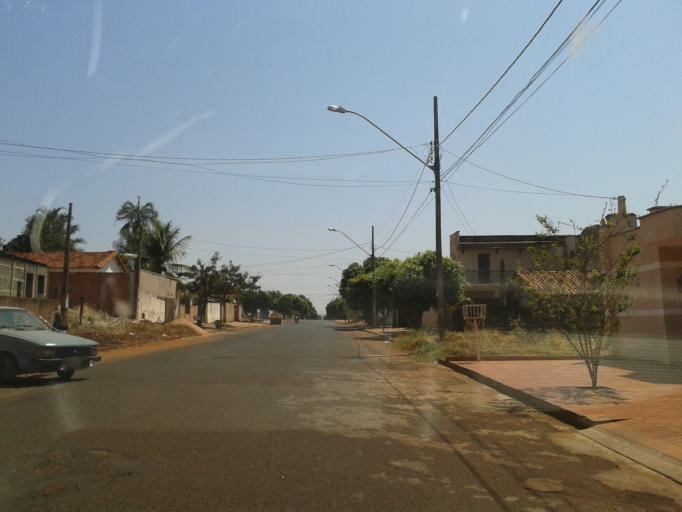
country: BR
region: Minas Gerais
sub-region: Ituiutaba
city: Ituiutaba
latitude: -18.9934
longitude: -49.4449
